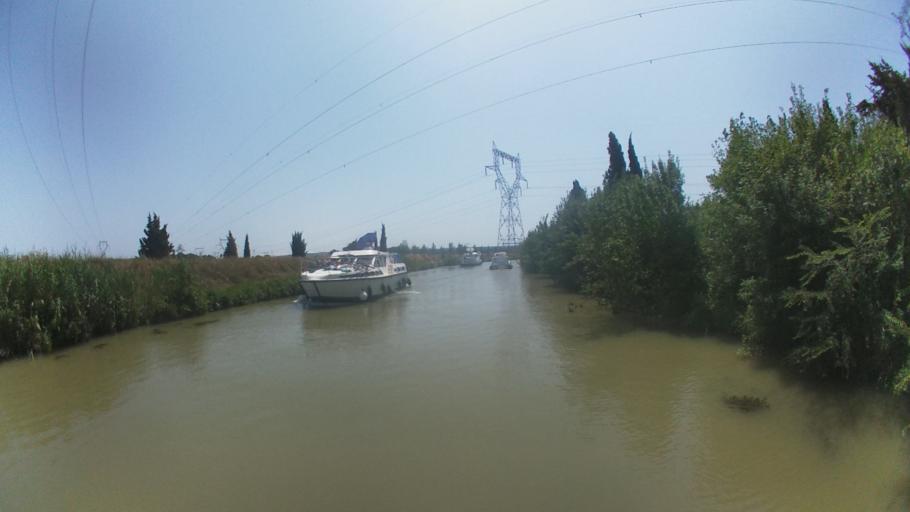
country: FR
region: Languedoc-Roussillon
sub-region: Departement de l'Aude
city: Azille
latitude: 43.2455
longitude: 2.6608
